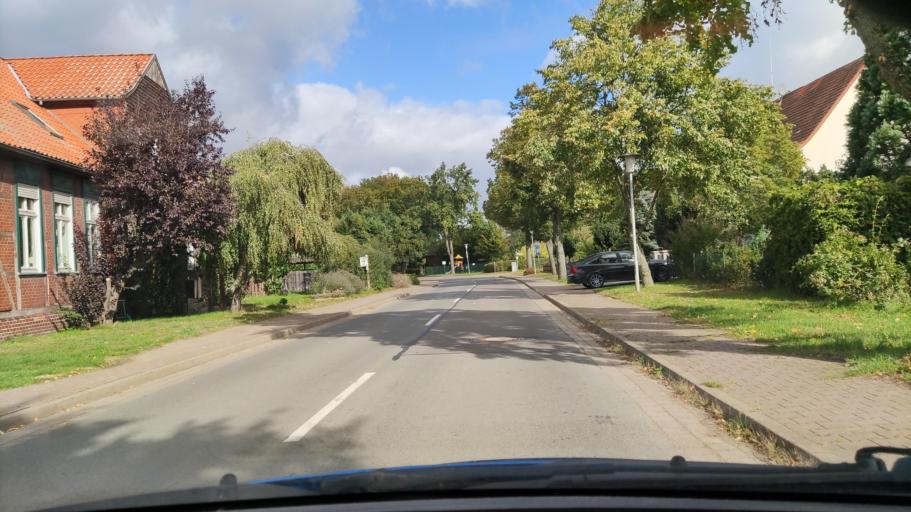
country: DE
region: Saxony-Anhalt
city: Salzwedel
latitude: 52.8546
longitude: 11.2075
